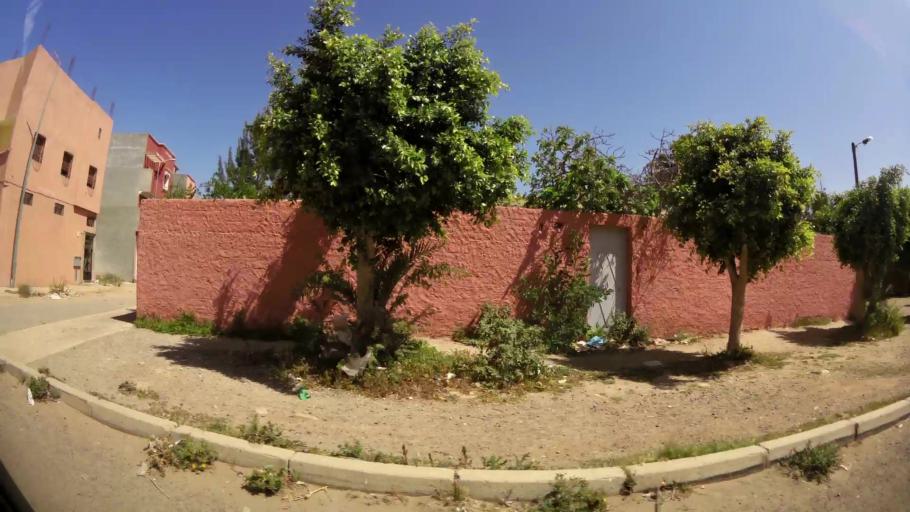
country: MA
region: Souss-Massa-Draa
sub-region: Inezgane-Ait Mellou
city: Inezgane
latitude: 30.3362
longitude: -9.5109
